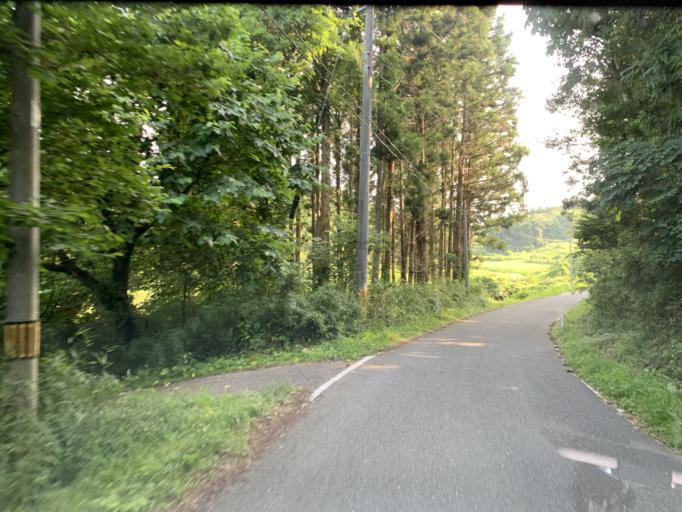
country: JP
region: Iwate
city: Ichinoseki
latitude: 38.8560
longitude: 141.1169
